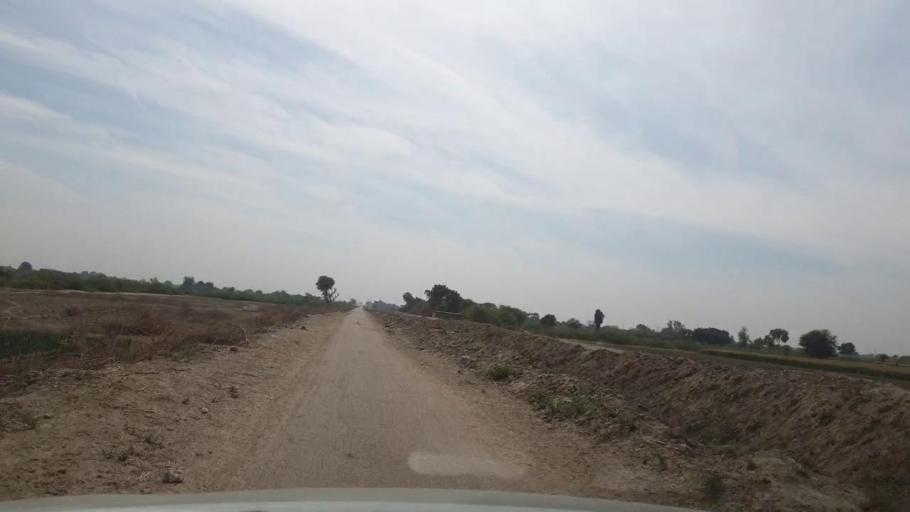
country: PK
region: Sindh
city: Nabisar
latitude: 25.0723
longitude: 69.5789
